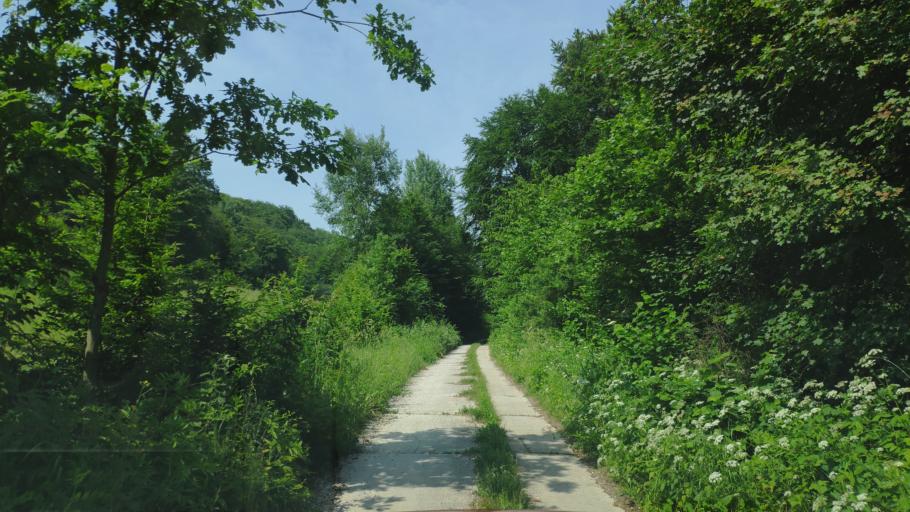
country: SK
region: Presovsky
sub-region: Okres Presov
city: Presov
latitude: 48.9692
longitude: 21.1452
